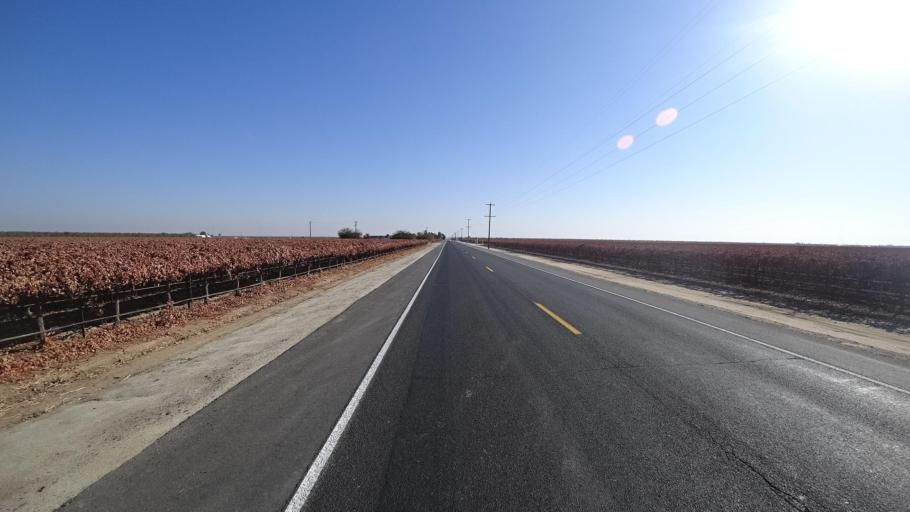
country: US
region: California
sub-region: Kern County
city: McFarland
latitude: 35.7178
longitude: -119.2652
